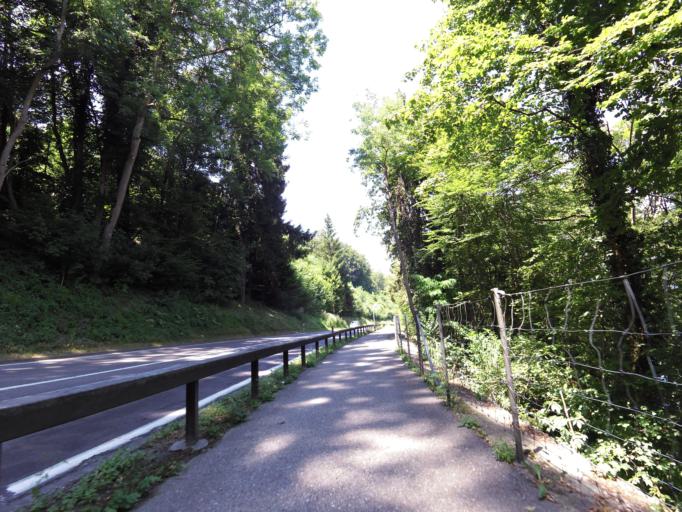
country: CH
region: Aargau
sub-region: Bezirk Bremgarten
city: Bremgarten
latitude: 47.3388
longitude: 8.3358
